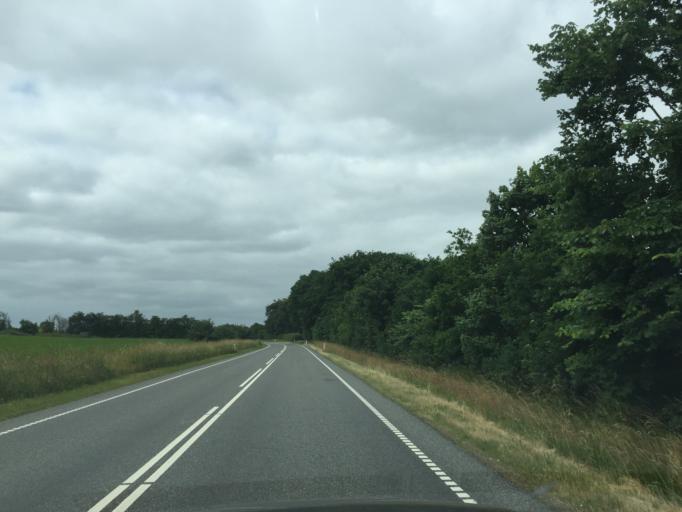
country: DK
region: South Denmark
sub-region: Vejen Kommune
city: Brorup
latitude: 55.4164
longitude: 8.9481
